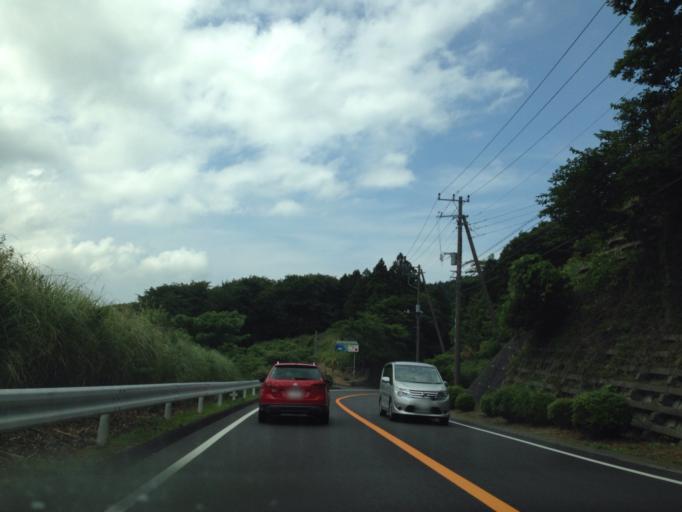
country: JP
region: Shizuoka
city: Heda
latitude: 34.9227
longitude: 138.8271
